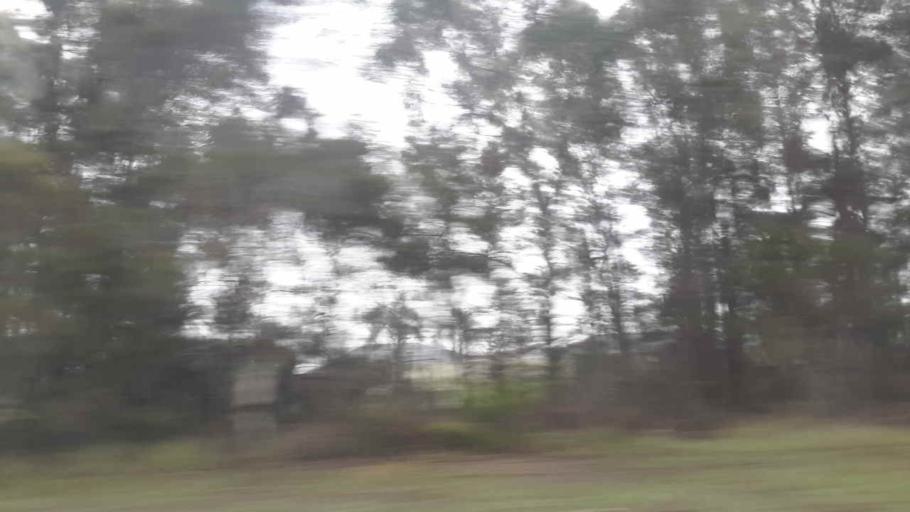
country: AU
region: New South Wales
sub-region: Penrith Municipality
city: Werrington Downs
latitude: -33.7065
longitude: 150.7236
